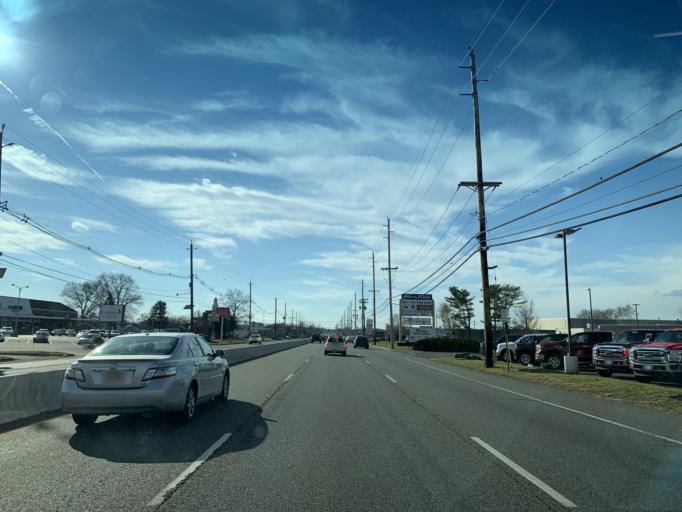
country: US
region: New Jersey
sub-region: Burlington County
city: Edgewater Park
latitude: 40.0488
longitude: -74.9003
